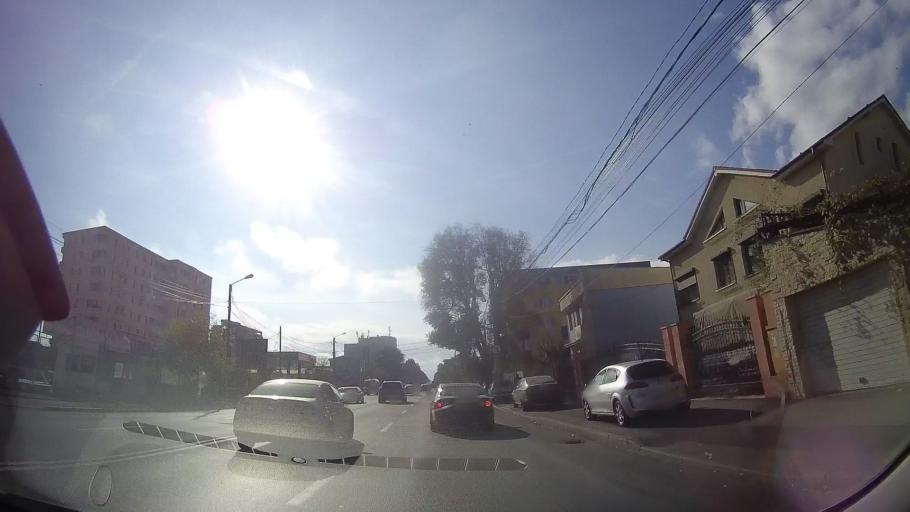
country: RO
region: Constanta
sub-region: Municipiul Constanta
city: Constanta
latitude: 44.1441
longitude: 28.6237
